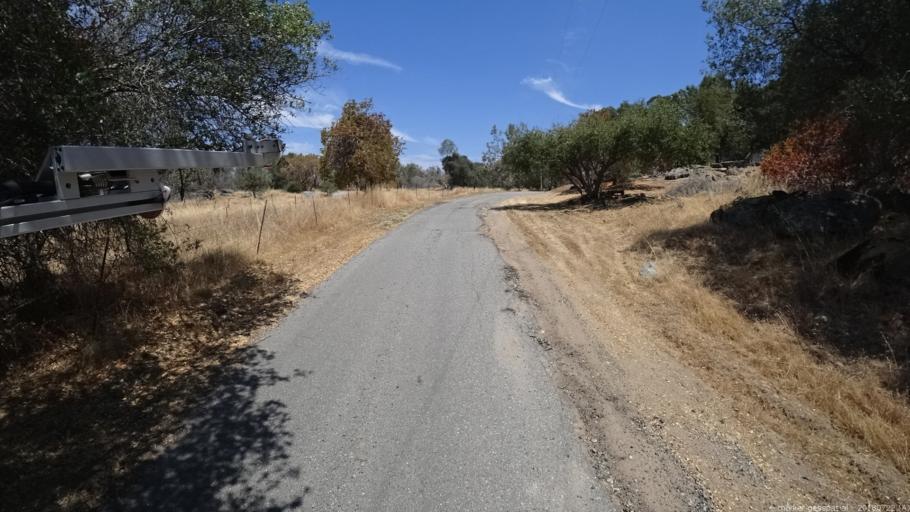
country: US
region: California
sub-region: Madera County
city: Coarsegold
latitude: 37.2690
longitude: -119.7322
